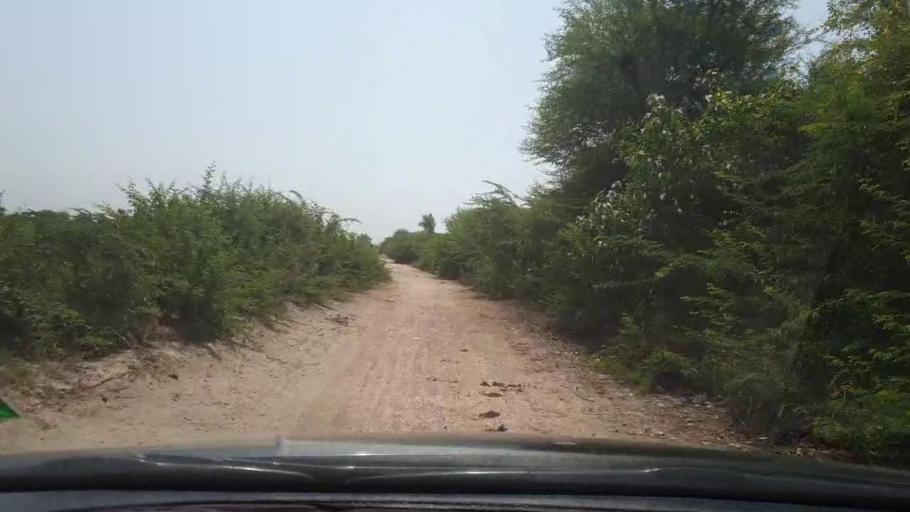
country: PK
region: Sindh
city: Tando Bago
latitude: 24.7805
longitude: 69.1826
